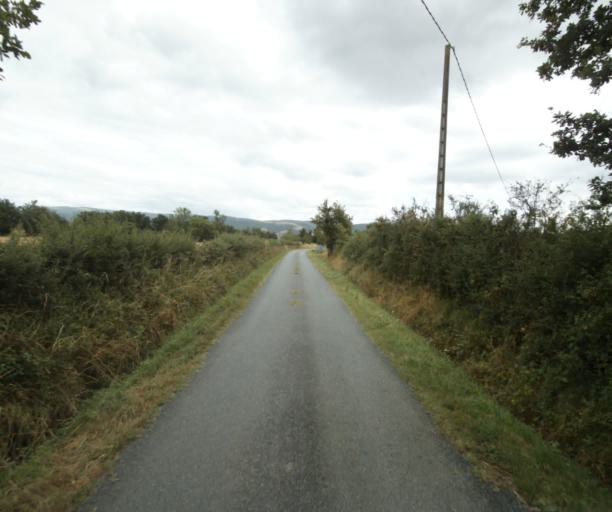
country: FR
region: Midi-Pyrenees
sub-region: Departement du Tarn
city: Soreze
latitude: 43.4806
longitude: 2.0459
